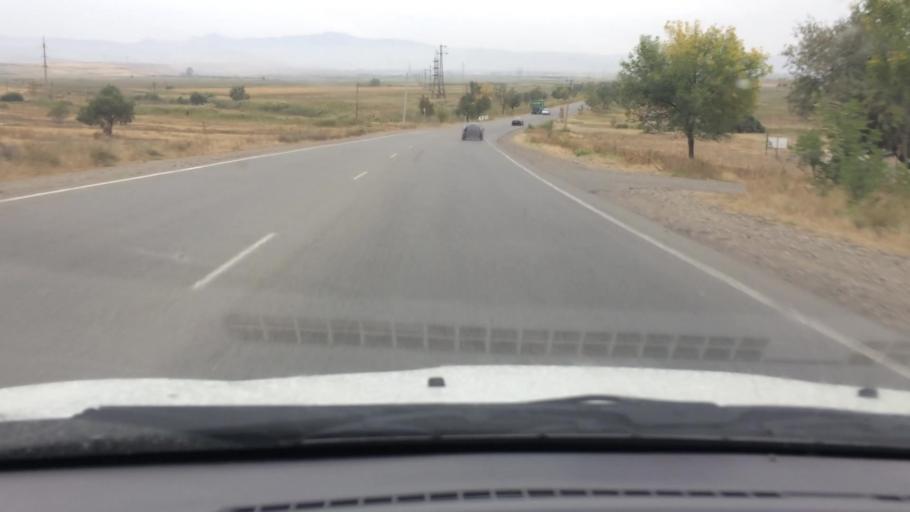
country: GE
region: Kvemo Kartli
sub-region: Marneuli
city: Marneuli
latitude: 41.5251
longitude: 44.7774
